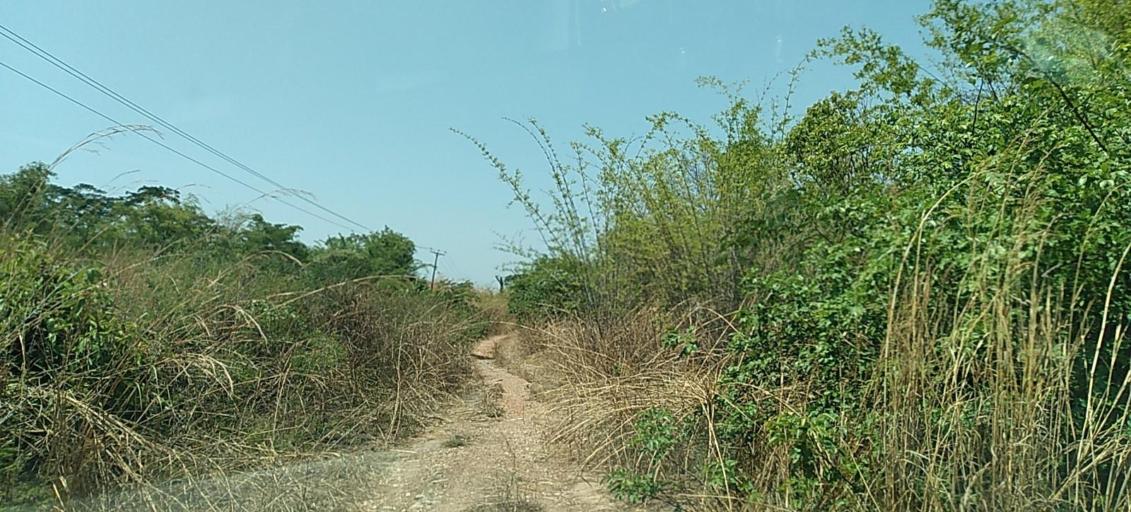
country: ZM
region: Copperbelt
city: Luanshya
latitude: -12.9802
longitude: 28.3293
